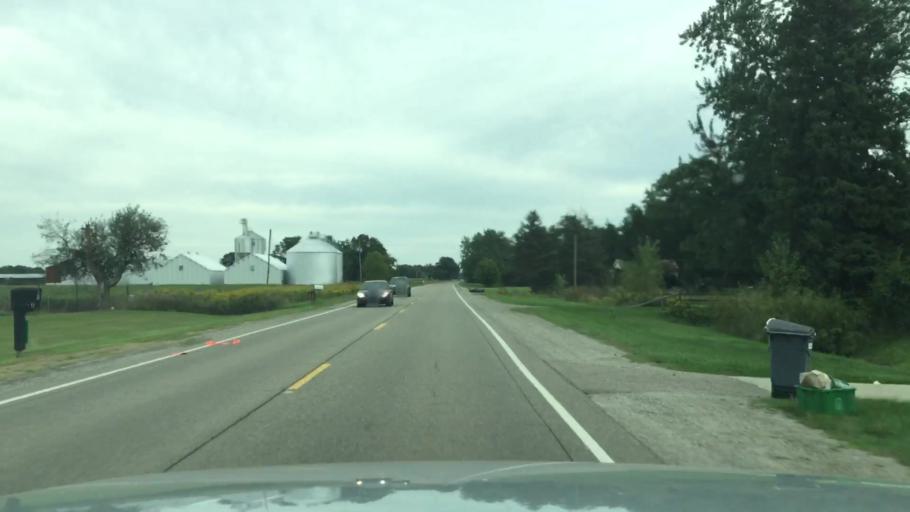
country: US
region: Michigan
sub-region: Genesee County
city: Swartz Creek
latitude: 42.9569
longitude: -83.9049
